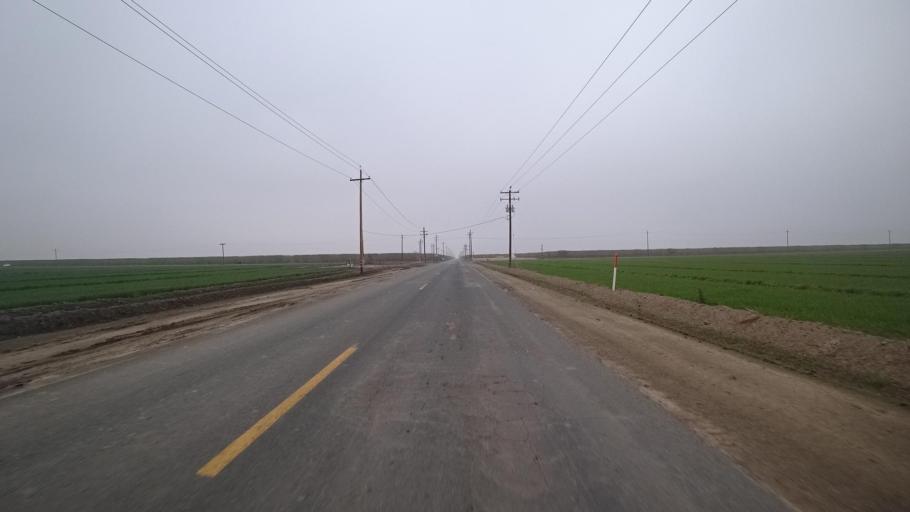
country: US
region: California
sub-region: Kern County
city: Wasco
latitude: 35.7177
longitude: -119.4350
